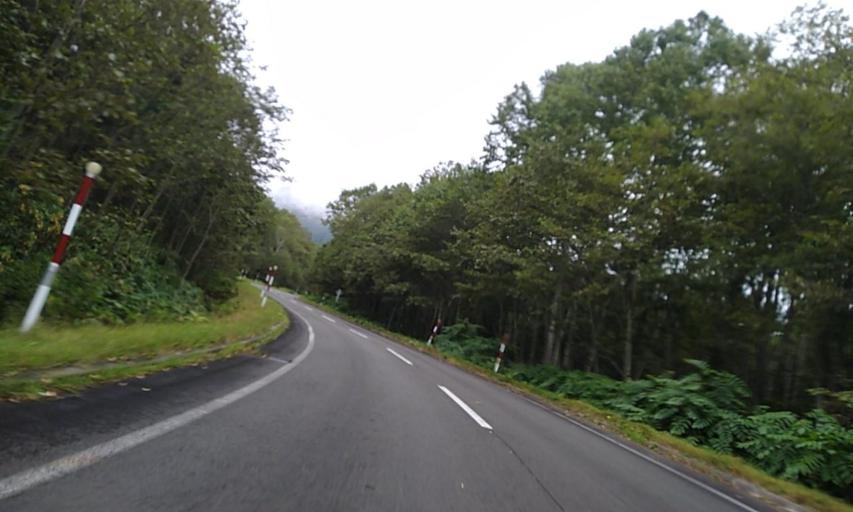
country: JP
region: Hokkaido
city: Bihoro
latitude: 43.5816
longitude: 144.2623
